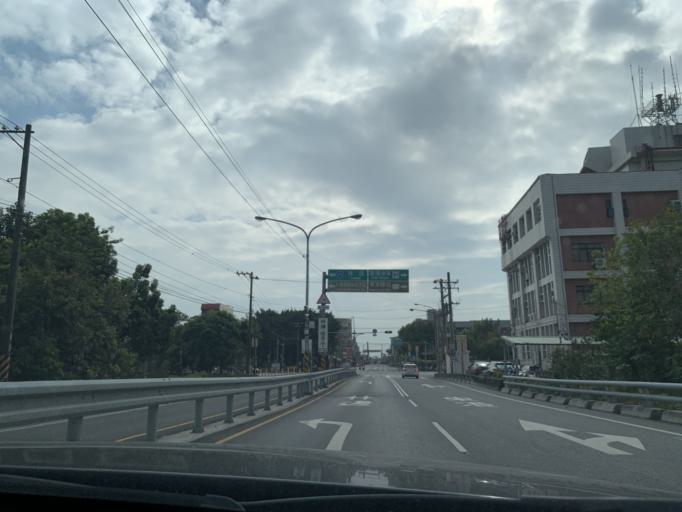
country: TW
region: Taiwan
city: Fengshan
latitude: 22.4637
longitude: 120.4623
